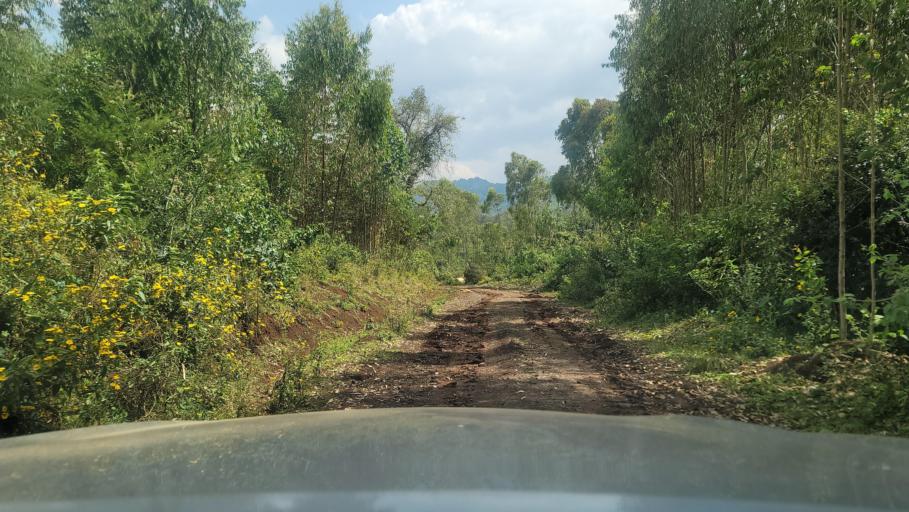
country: ET
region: Oromiya
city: Agaro
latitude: 7.7362
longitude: 36.2641
